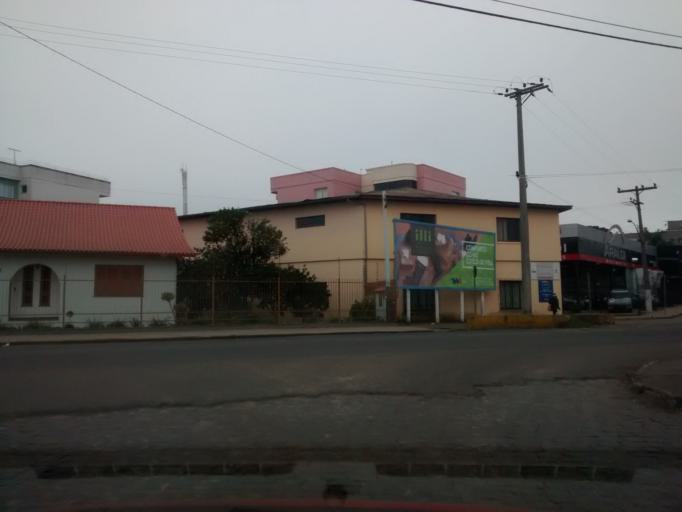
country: BR
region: Rio Grande do Sul
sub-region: Vacaria
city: Vacaria
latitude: -28.5070
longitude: -50.9416
